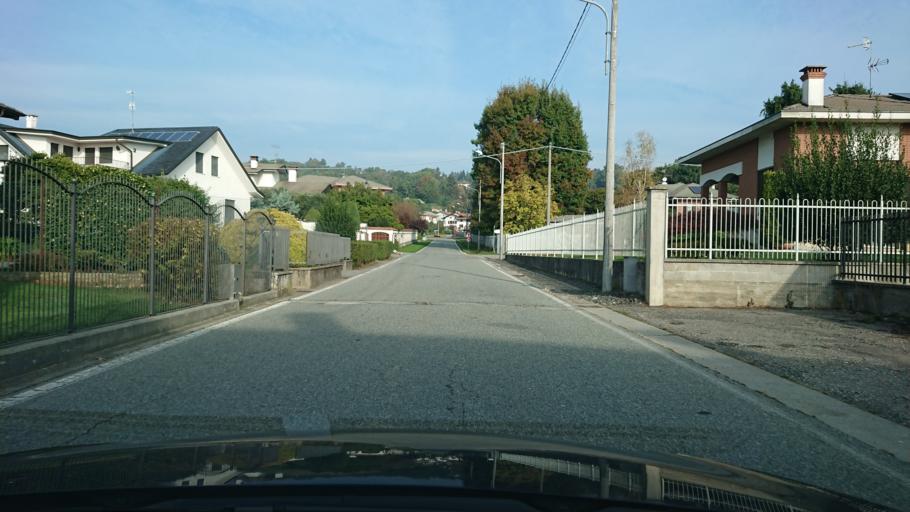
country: IT
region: Piedmont
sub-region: Provincia di Biella
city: Valdengo
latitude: 45.5698
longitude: 8.1311
